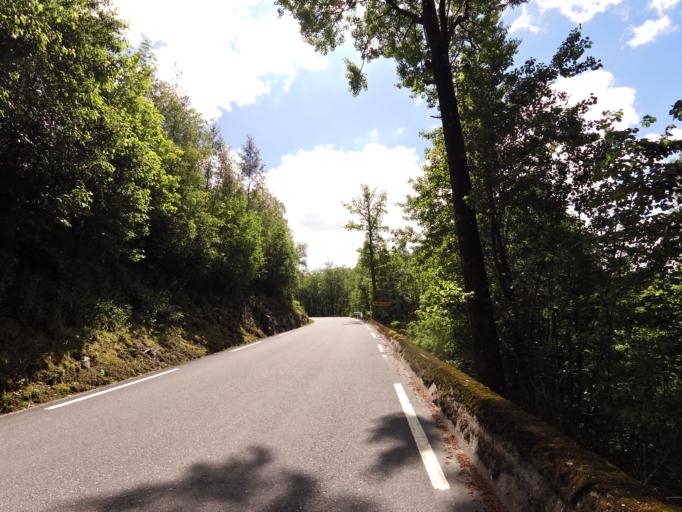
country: NO
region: Vest-Agder
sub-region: Kvinesdal
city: Liknes
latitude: 58.2895
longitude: 6.9388
